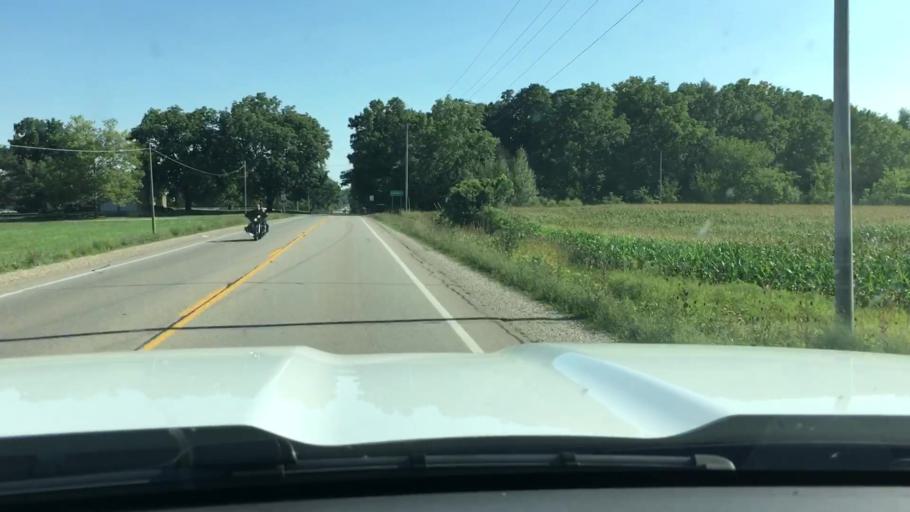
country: US
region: Michigan
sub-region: Ottawa County
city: Coopersville
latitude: 43.0217
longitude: -85.9561
